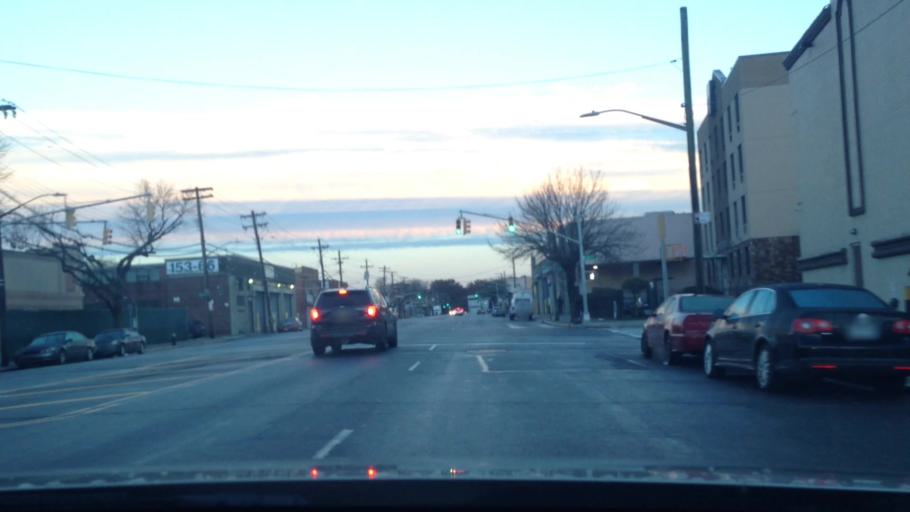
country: US
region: New York
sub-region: Queens County
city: Jamaica
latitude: 40.6684
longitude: -73.7813
